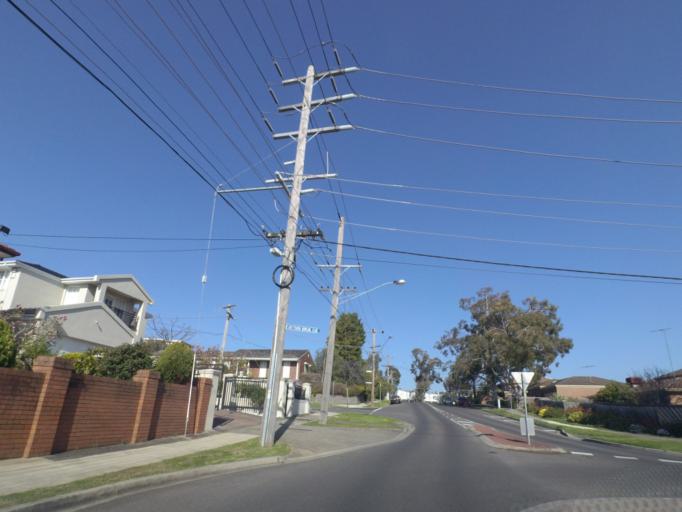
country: AU
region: Victoria
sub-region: Boroondara
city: Balwyn North
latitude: -37.7854
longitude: 145.1045
